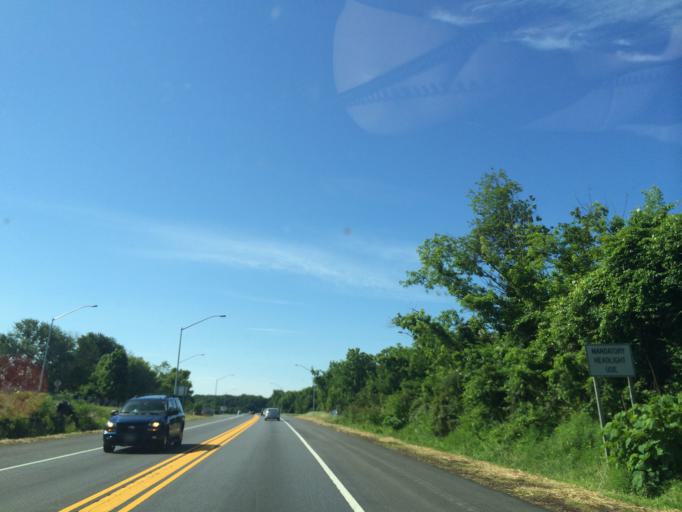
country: US
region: Maryland
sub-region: Howard County
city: Highland
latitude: 39.2288
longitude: -76.9732
